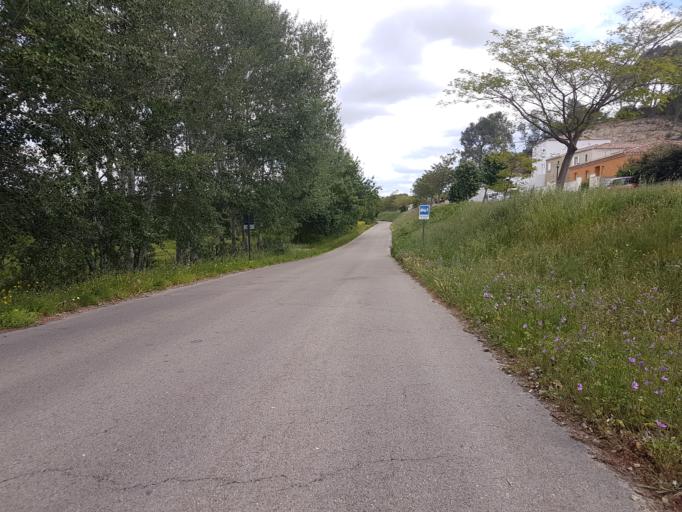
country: FR
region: Languedoc-Roussillon
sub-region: Departement du Gard
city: Beaucaire
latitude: 43.8189
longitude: 4.6349
